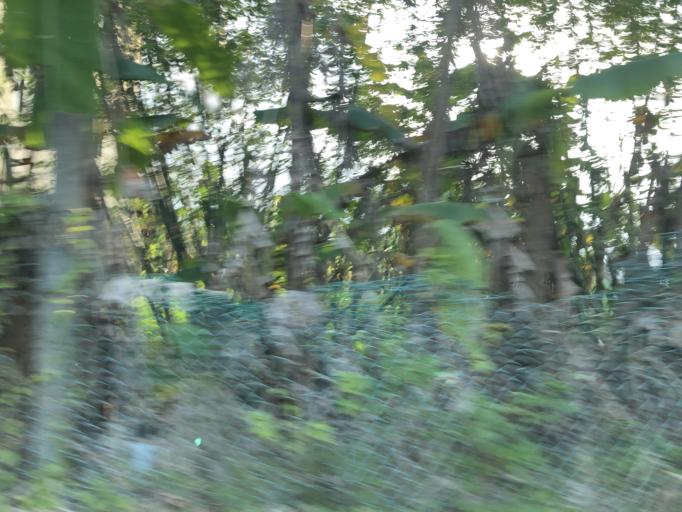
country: TW
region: Taiwan
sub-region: Keelung
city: Keelung
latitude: 25.2105
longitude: 121.6465
